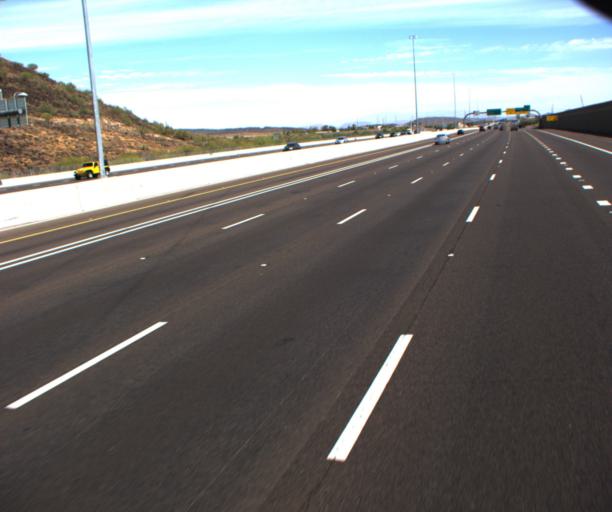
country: US
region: Arizona
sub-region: Maricopa County
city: Peoria
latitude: 33.6924
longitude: -112.1131
